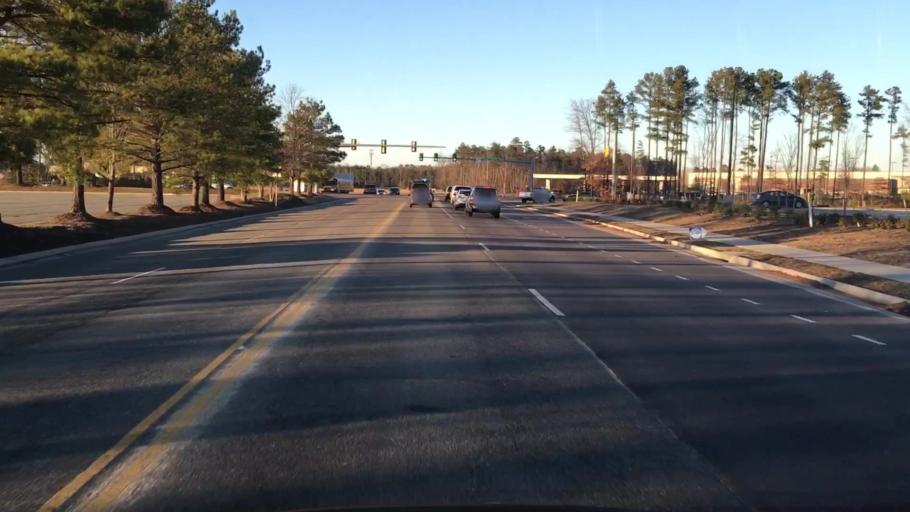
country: US
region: Virginia
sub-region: Chesterfield County
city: Bon Air
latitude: 37.5108
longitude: -77.6068
